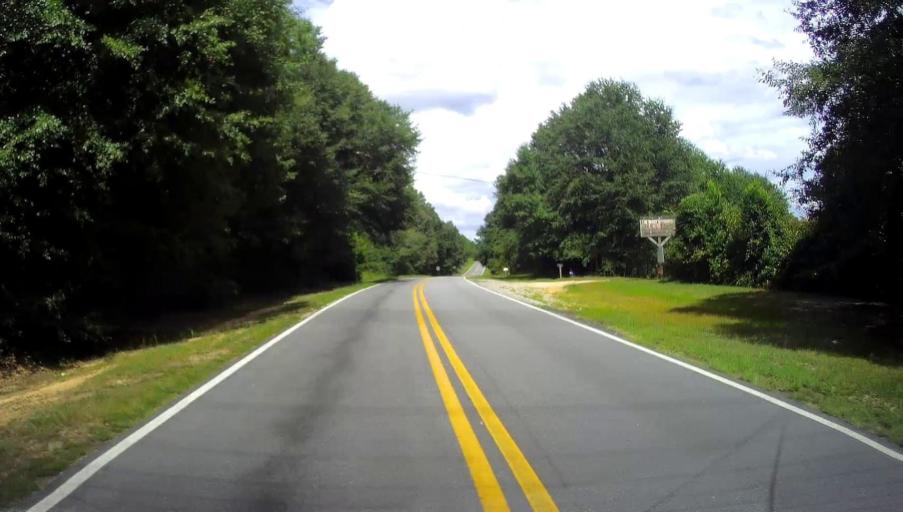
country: US
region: Georgia
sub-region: Chattahoochee County
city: Cusseta
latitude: 32.3066
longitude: -84.7676
